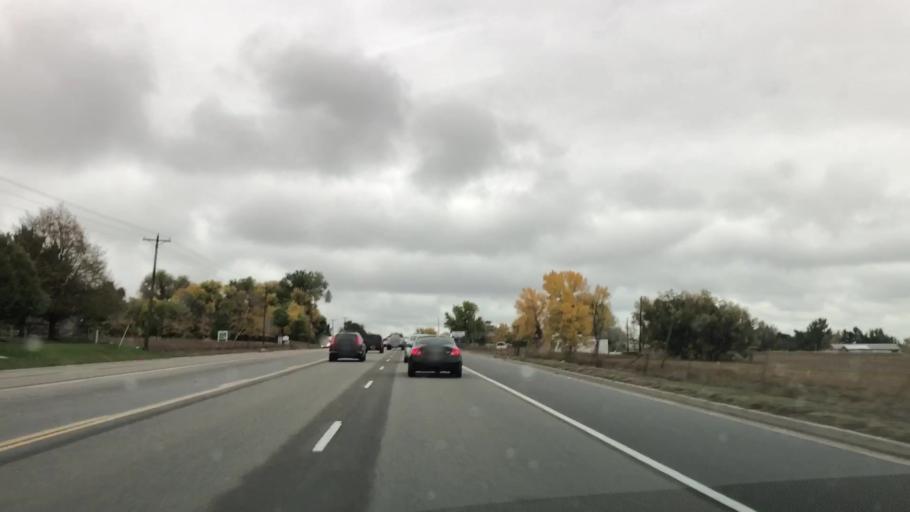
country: US
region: Colorado
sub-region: Larimer County
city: Loveland
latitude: 40.4892
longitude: -105.0770
